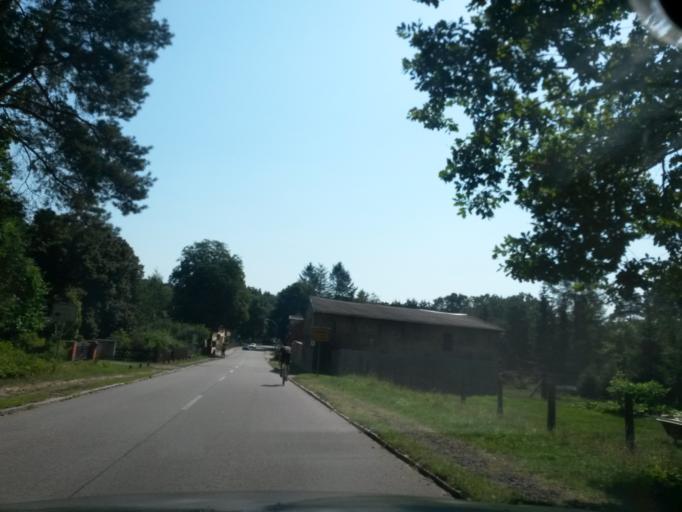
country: DE
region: Brandenburg
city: Marienwerder
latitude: 52.8933
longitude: 13.6363
